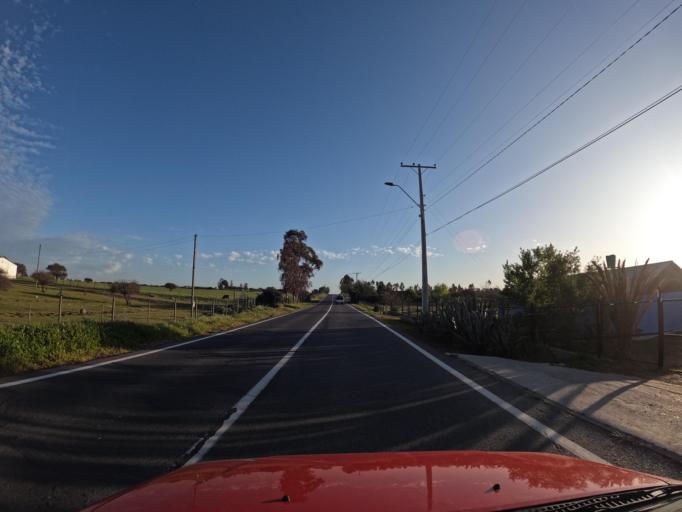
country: CL
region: O'Higgins
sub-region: Provincia de Colchagua
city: Santa Cruz
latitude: -34.2251
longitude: -71.7239
